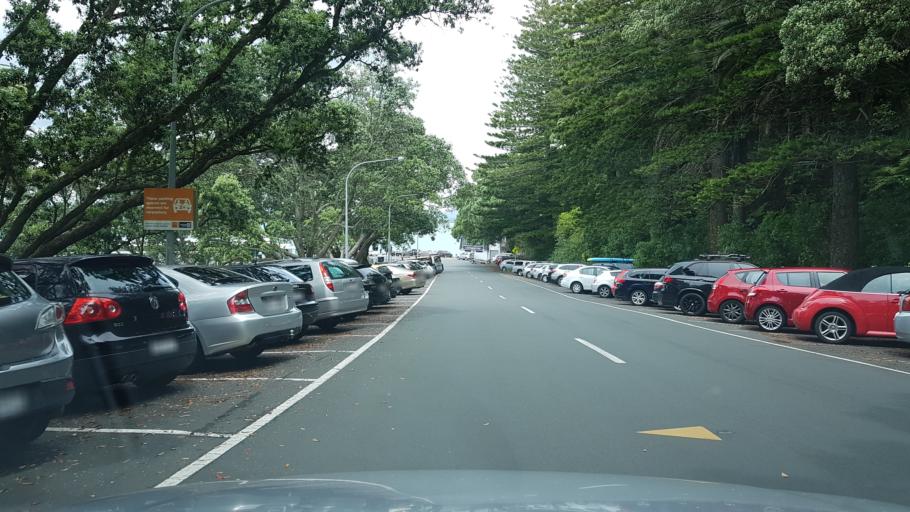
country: NZ
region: Auckland
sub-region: Auckland
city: North Shore
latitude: -36.8216
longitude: 174.7346
